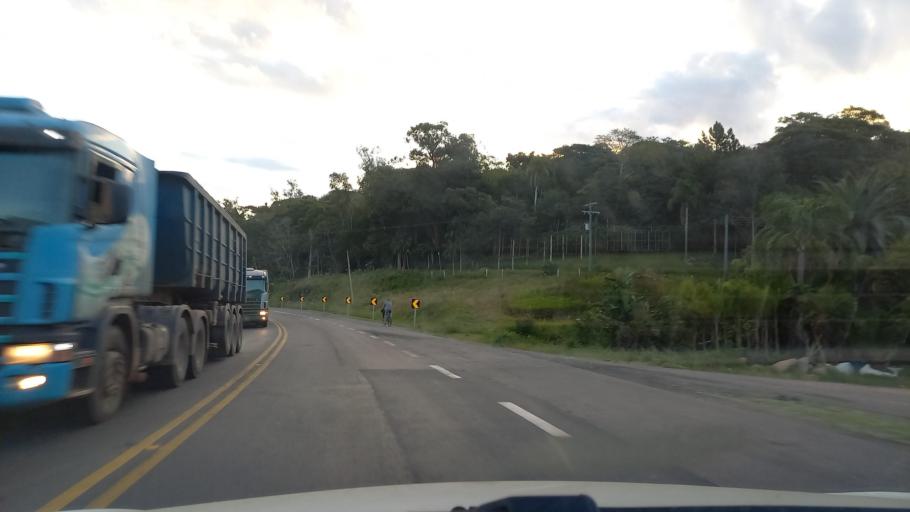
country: BR
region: Rio Grande do Sul
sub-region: Santa Cruz Do Sul
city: Santa Cruz do Sul
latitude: -29.6846
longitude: -52.4419
